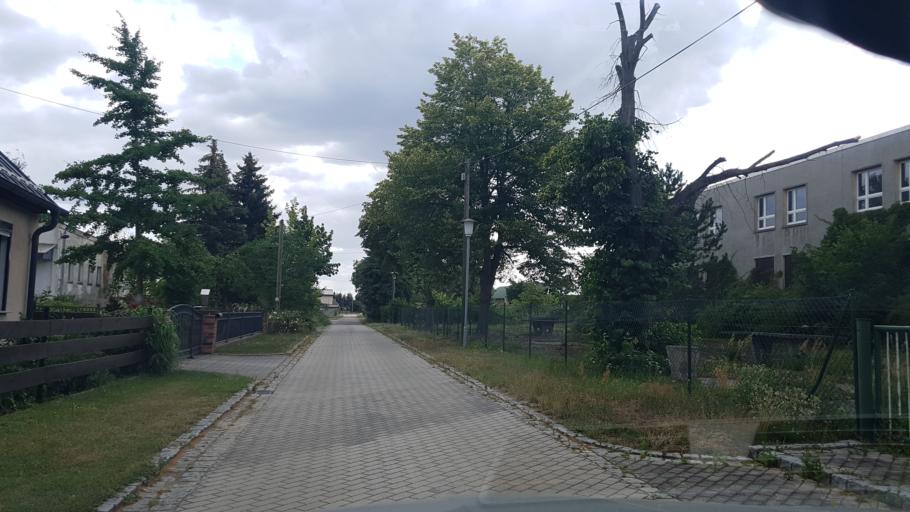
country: DE
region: Brandenburg
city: Bad Liebenwerda
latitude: 51.4937
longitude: 13.4086
